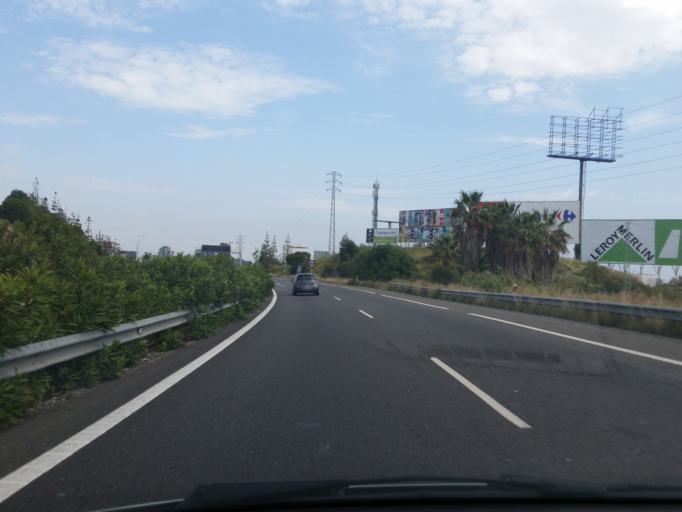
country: ES
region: Andalusia
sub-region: Provincia de Malaga
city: Torremolinos
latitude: 36.6443
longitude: -4.4927
